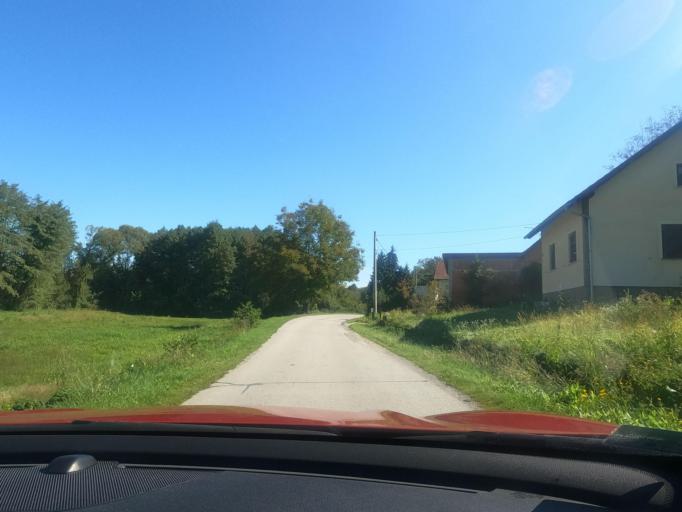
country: HR
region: Sisacko-Moslavacka
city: Petrinja
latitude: 45.4138
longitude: 16.2560
